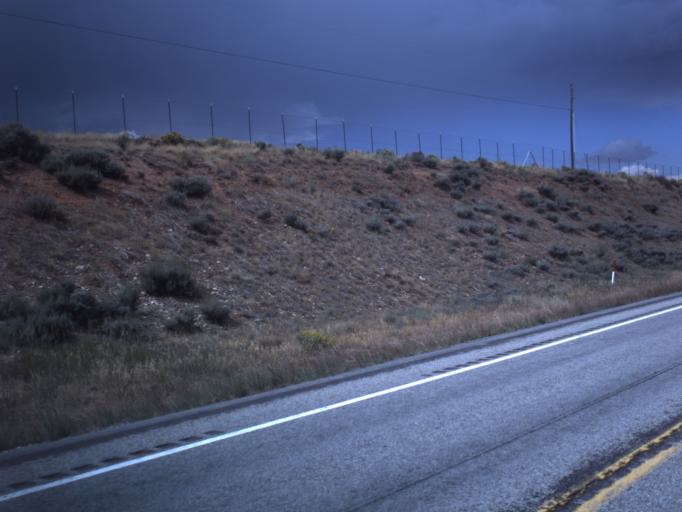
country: US
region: Utah
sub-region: San Juan County
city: Monticello
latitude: 37.8243
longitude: -109.3369
